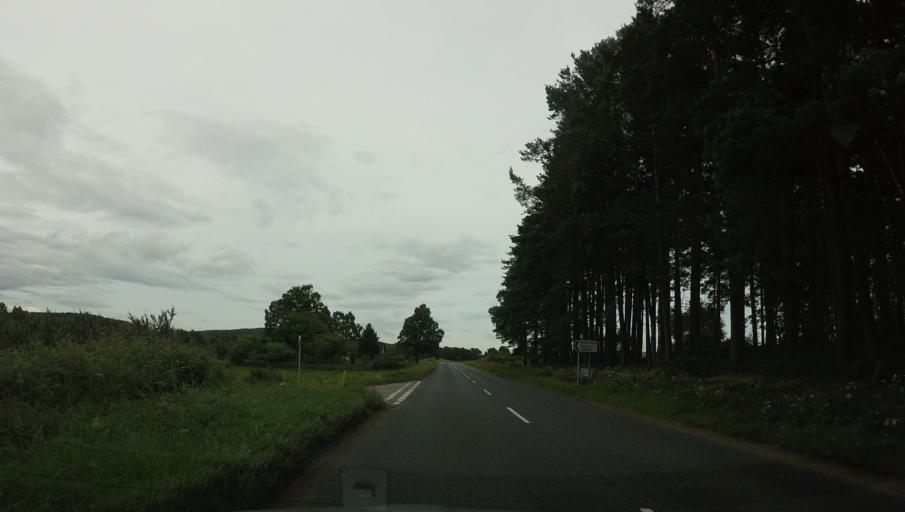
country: GB
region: Scotland
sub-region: Aberdeenshire
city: Aboyne
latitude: 57.0887
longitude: -2.7456
